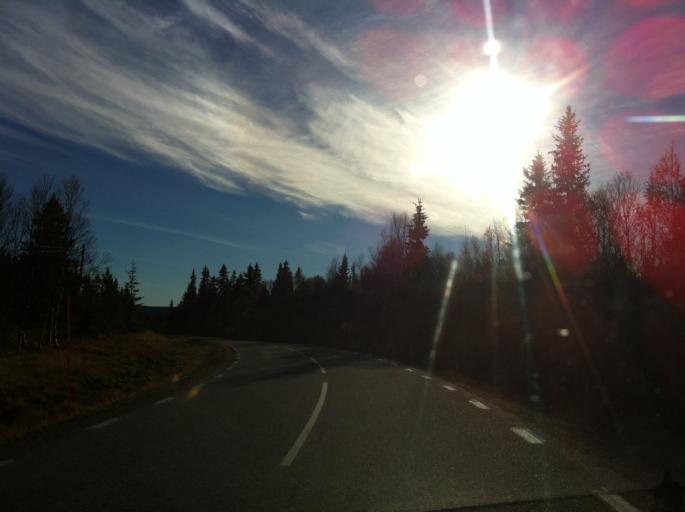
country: NO
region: Hedmark
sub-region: Engerdal
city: Engerdal
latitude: 62.0846
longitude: 12.3097
